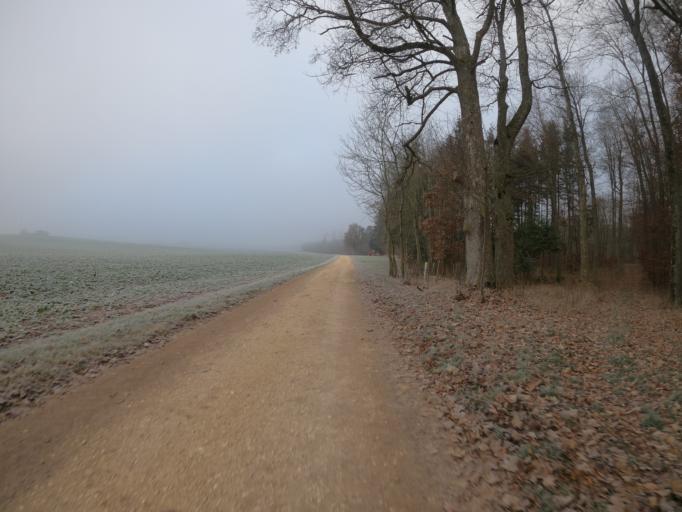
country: DE
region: Baden-Wuerttemberg
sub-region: Tuebingen Region
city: Beimerstetten
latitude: 48.4900
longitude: 9.9681
